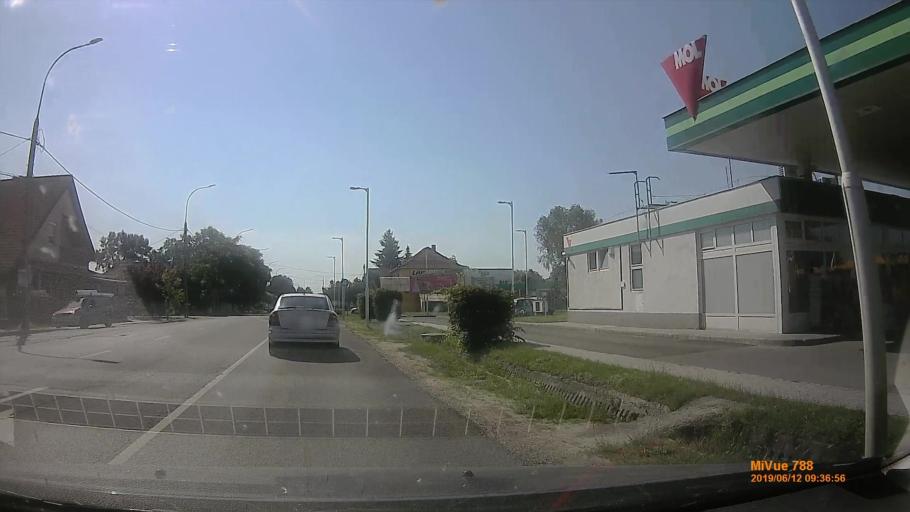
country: HU
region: Pest
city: Gyal
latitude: 47.3778
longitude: 19.2199
